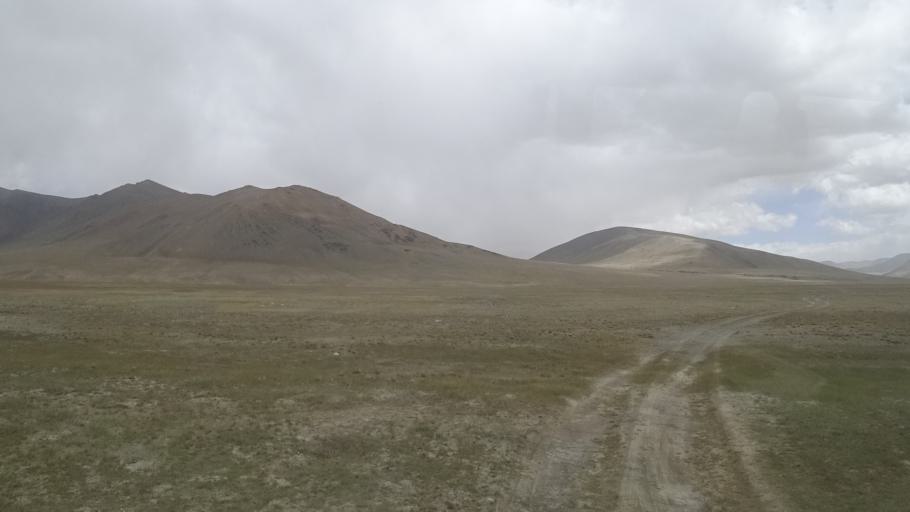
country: TJ
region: Gorno-Badakhshan
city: Murghob
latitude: 37.4902
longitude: 74.0228
